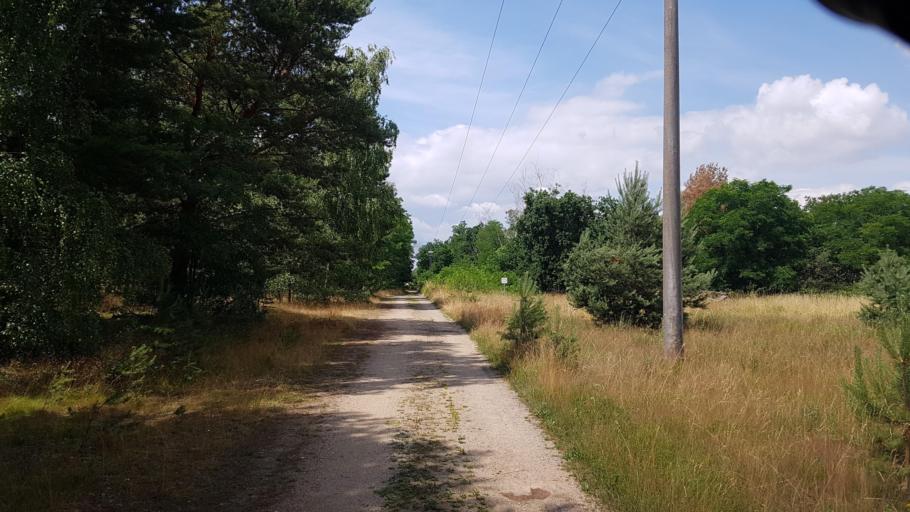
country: DE
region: Brandenburg
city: Crinitz
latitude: 51.7550
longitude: 13.8179
